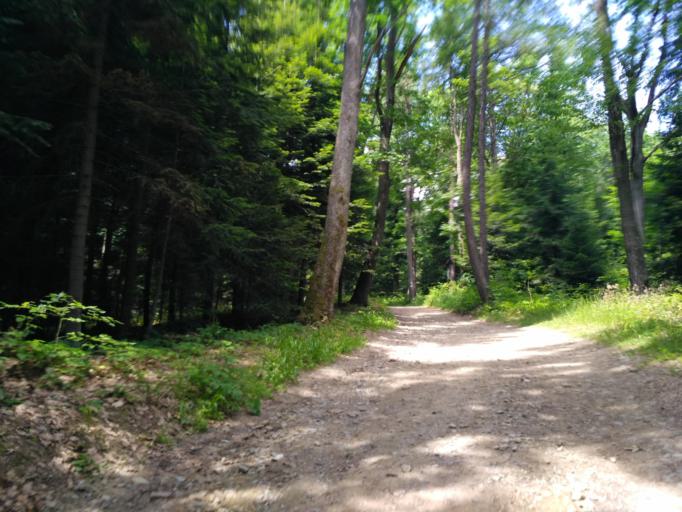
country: PL
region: Subcarpathian Voivodeship
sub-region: Powiat jasielski
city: Brzyska
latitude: 49.8127
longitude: 21.3539
